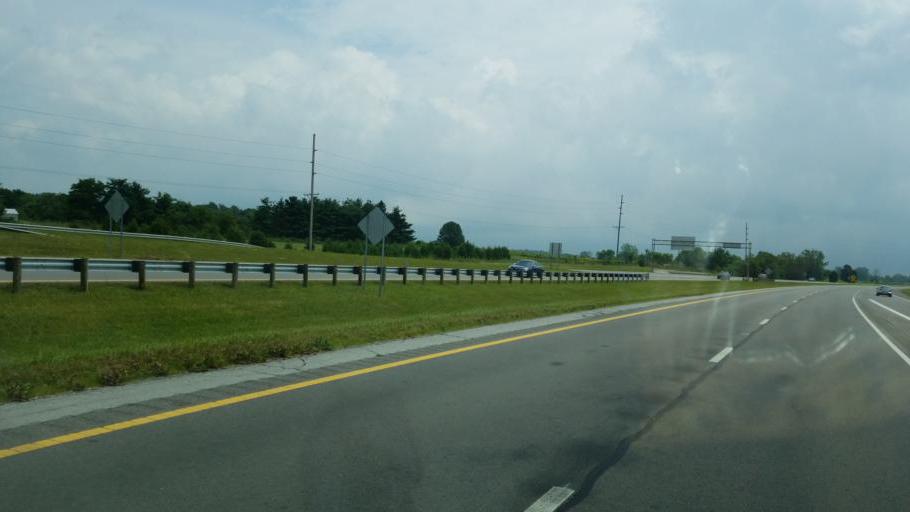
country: US
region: Ohio
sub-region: Logan County
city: Northwood
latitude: 40.4337
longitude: -83.8043
